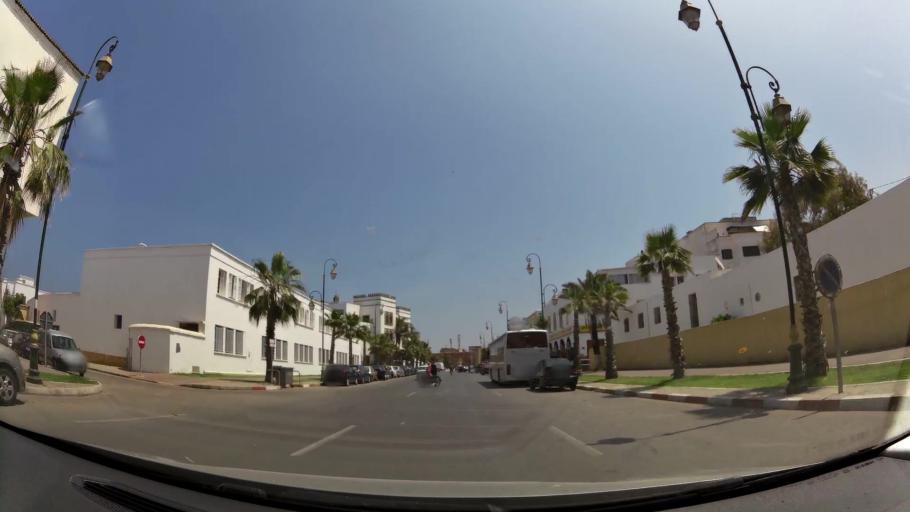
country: MA
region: Rabat-Sale-Zemmour-Zaer
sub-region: Rabat
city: Rabat
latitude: 34.0252
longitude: -6.8437
